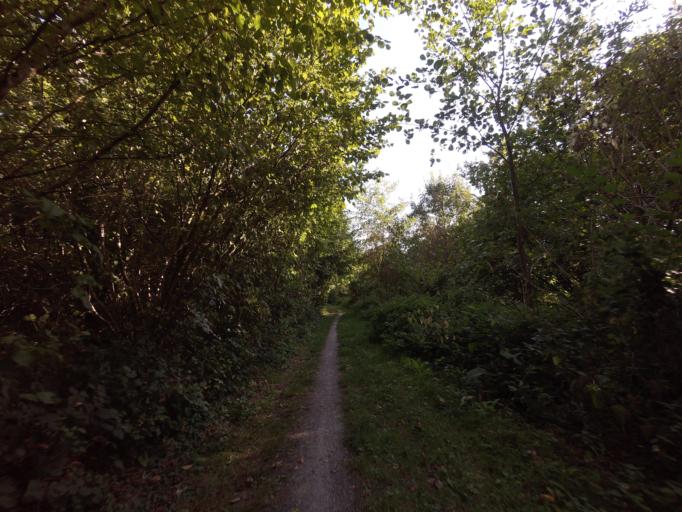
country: BE
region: Flanders
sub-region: Provincie Vlaams-Brabant
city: Kampenhout
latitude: 50.9380
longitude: 4.5846
